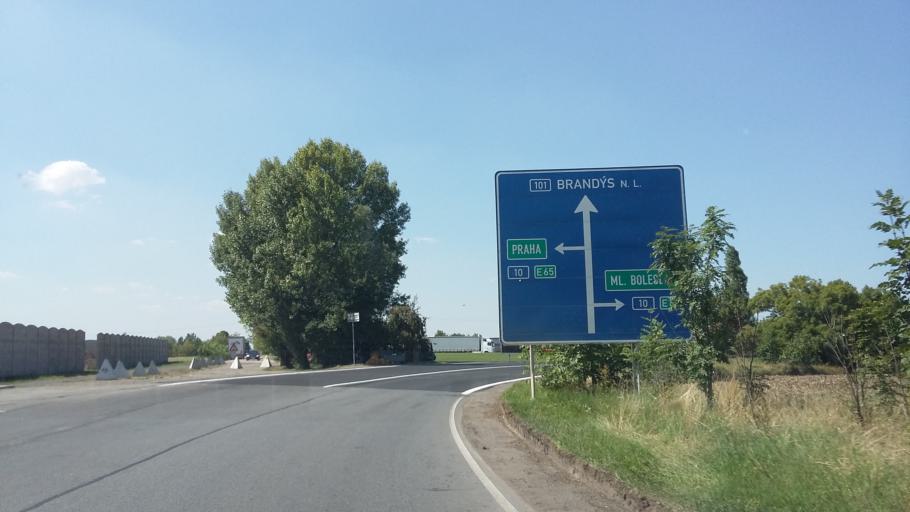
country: CZ
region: Central Bohemia
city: Brandys nad Labem-Stara Boleslav
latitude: 50.1662
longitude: 14.6758
